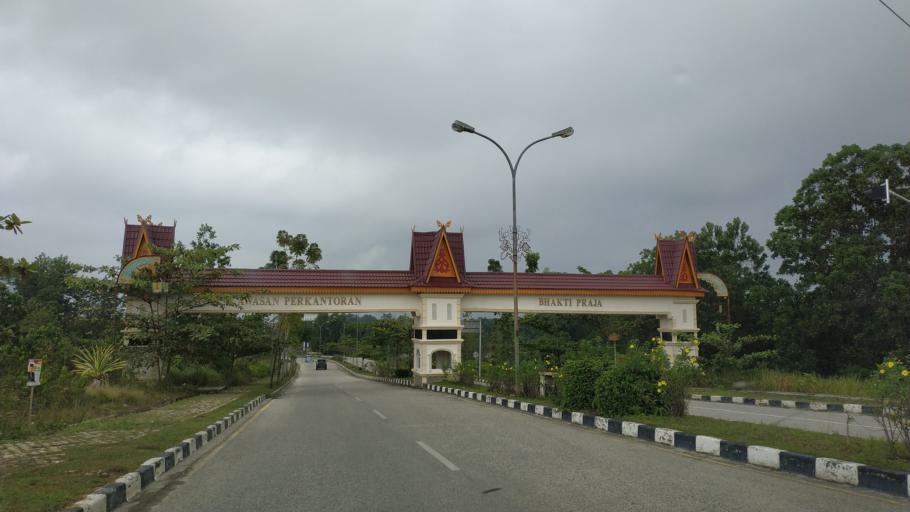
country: ID
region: Riau
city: Pangkalanbunut
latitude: 0.3864
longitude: 101.8257
